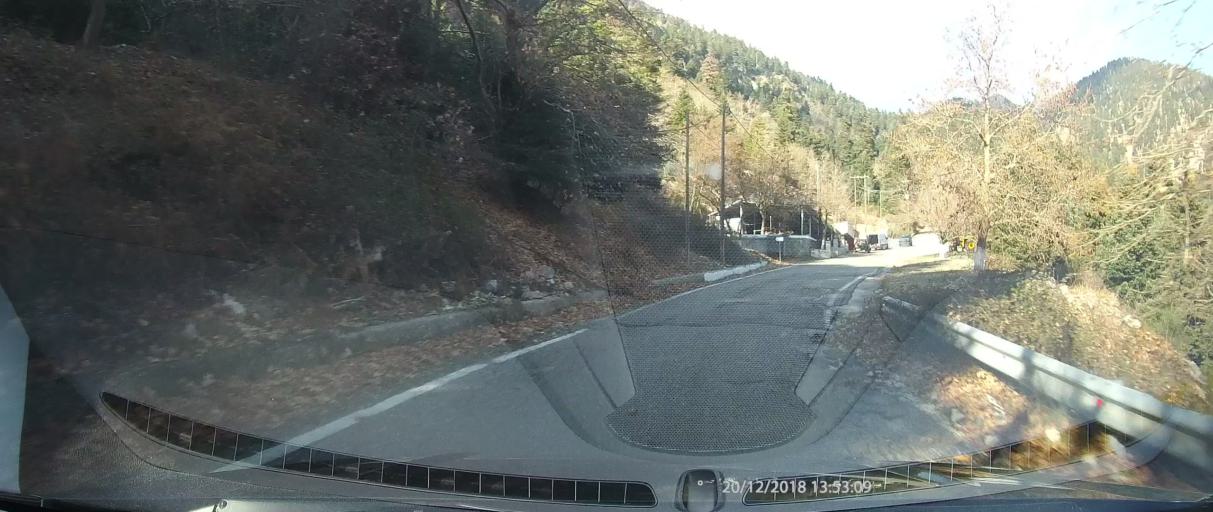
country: GR
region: West Greece
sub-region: Nomos Aitolias kai Akarnanias
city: Paravola
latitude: 38.7094
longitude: 21.6062
